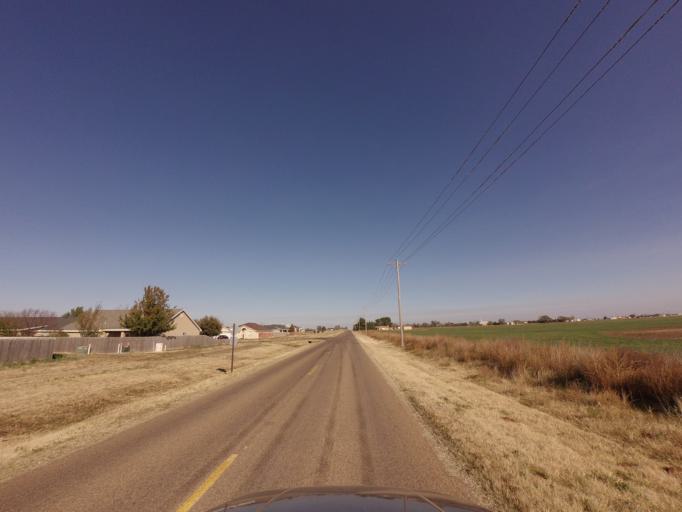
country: US
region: New Mexico
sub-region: Curry County
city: Clovis
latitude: 34.4141
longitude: -103.1607
